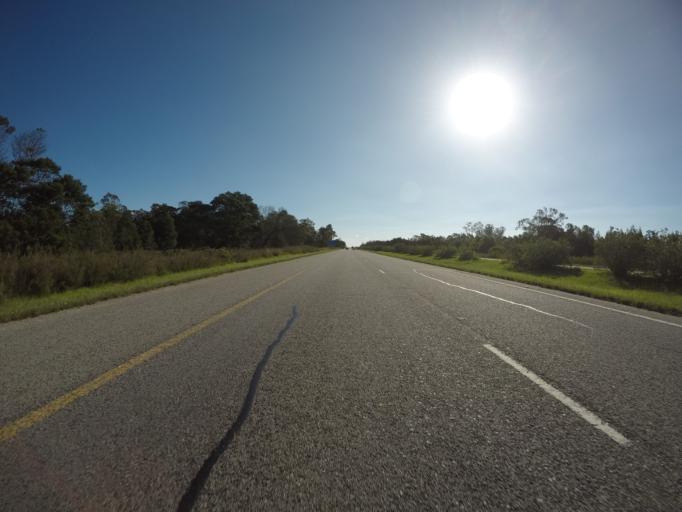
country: ZA
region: Eastern Cape
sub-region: Nelson Mandela Bay Metropolitan Municipality
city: Port Elizabeth
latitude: -33.9438
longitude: 25.3925
